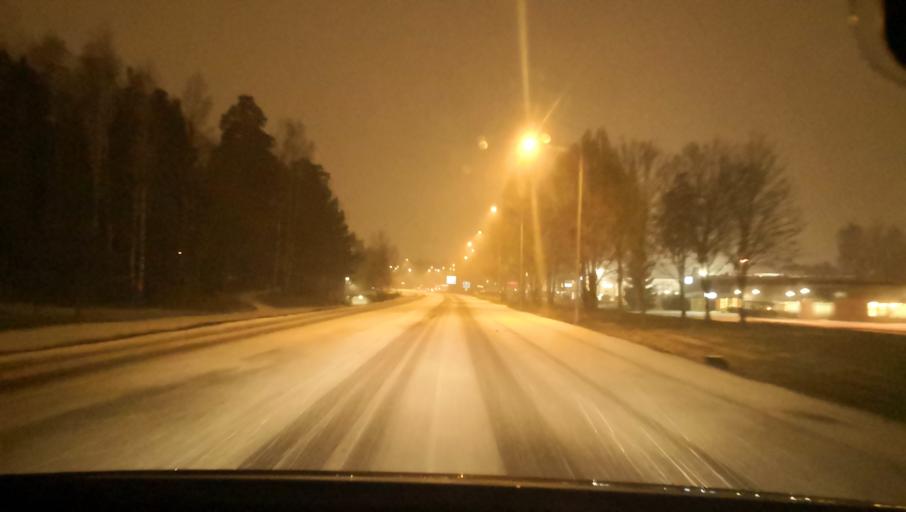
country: SE
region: Vaestmanland
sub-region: Vasteras
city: Hokasen
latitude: 59.6354
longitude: 16.5854
